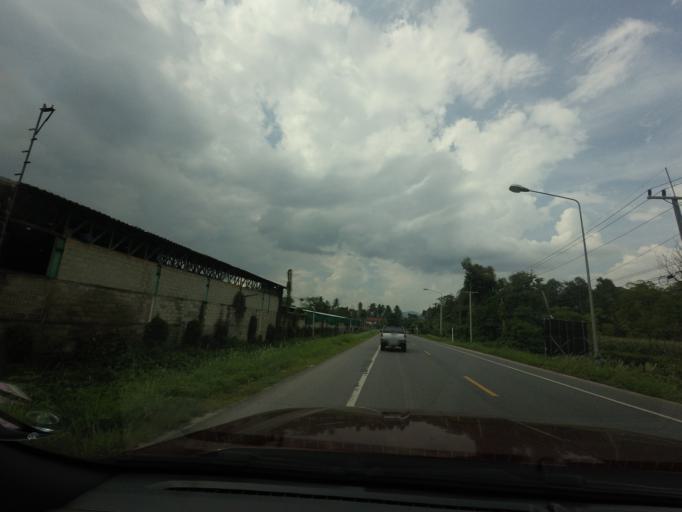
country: TH
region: Yala
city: Ban Nang Sata
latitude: 6.2661
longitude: 101.2777
